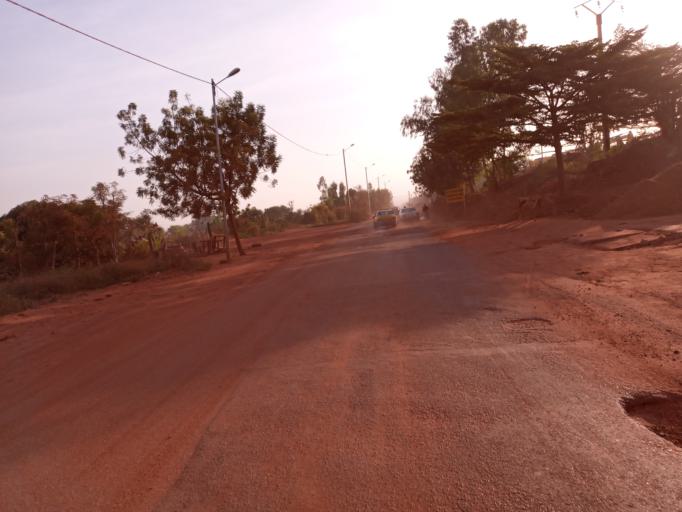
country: ML
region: Bamako
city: Bamako
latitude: 12.6344
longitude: -7.9360
